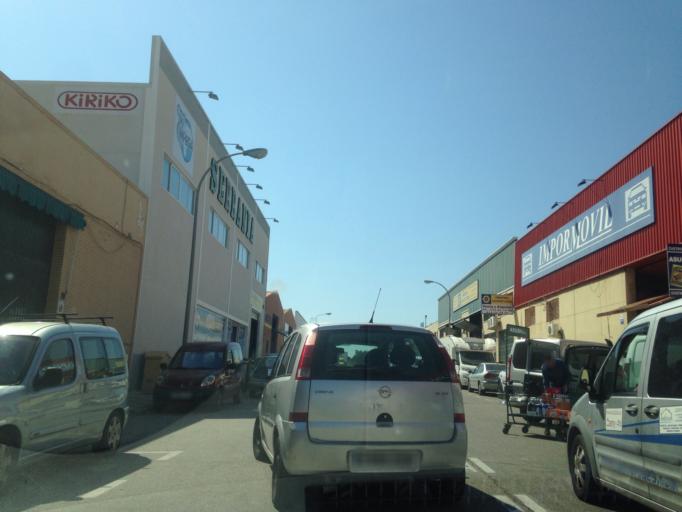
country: ES
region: Andalusia
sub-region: Provincia de Malaga
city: Malaga
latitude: 36.7034
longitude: -4.4766
